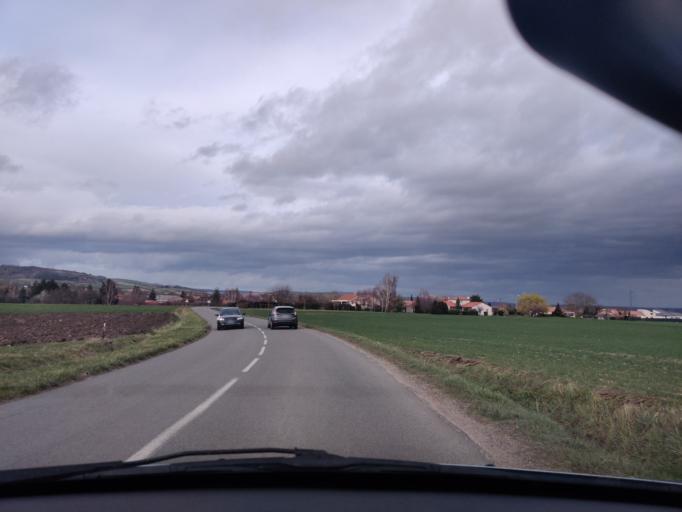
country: FR
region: Auvergne
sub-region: Departement du Puy-de-Dome
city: Saint-Bonnet-pres-Riom
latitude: 45.9285
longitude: 3.0898
